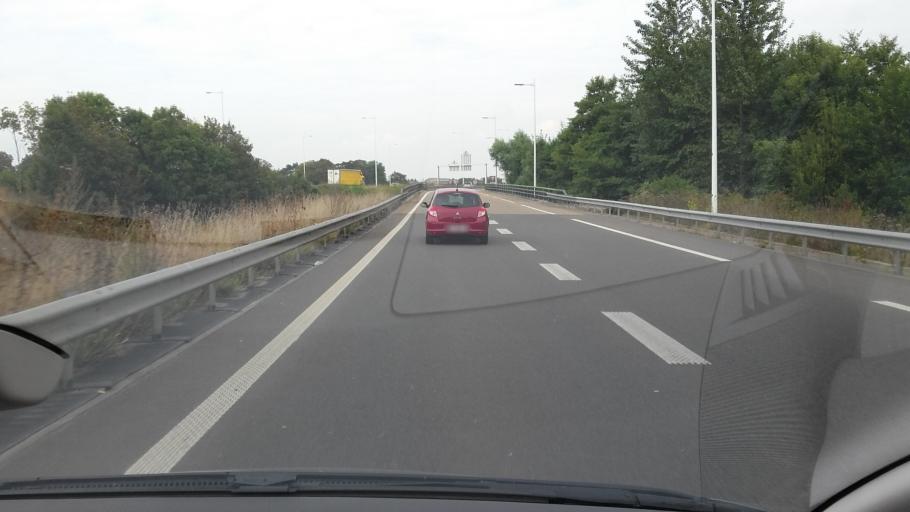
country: FR
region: Champagne-Ardenne
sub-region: Departement de la Marne
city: Cormontreuil
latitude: 49.2247
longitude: 4.0670
